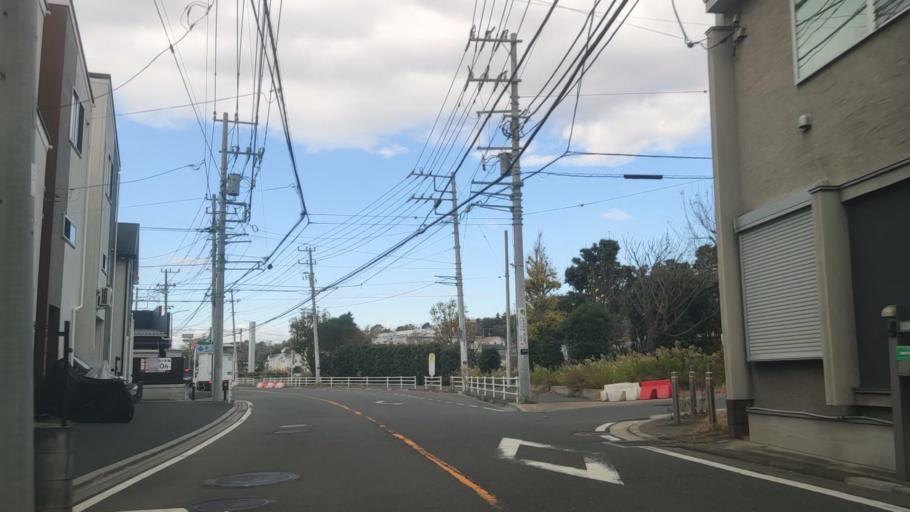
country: JP
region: Kanagawa
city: Minami-rinkan
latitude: 35.4264
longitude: 139.5286
